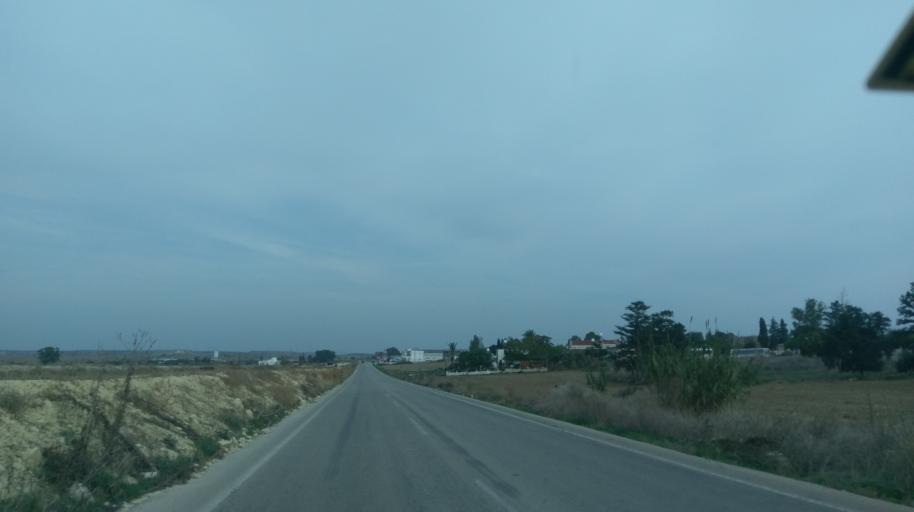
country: CY
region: Ammochostos
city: Trikomo
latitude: 35.3648
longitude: 34.0201
